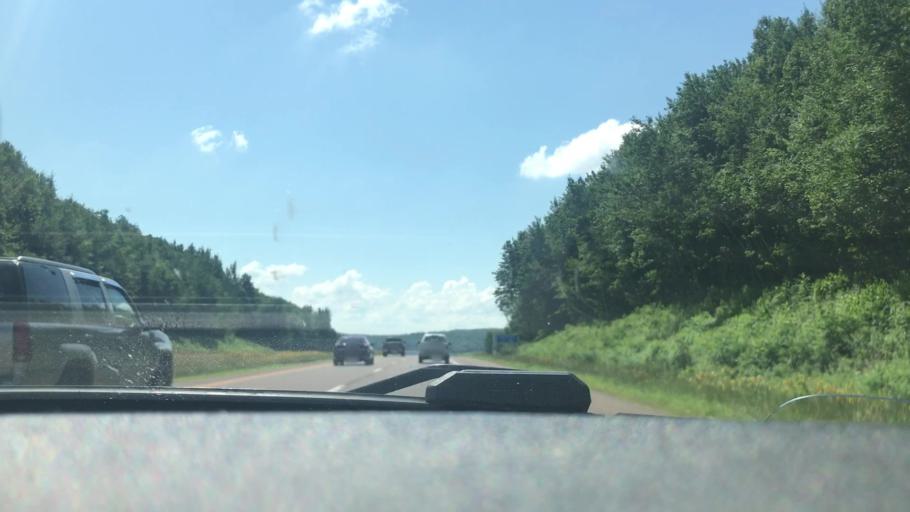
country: US
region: Wisconsin
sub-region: Chippewa County
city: Chippewa Falls
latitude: 44.9756
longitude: -91.4349
